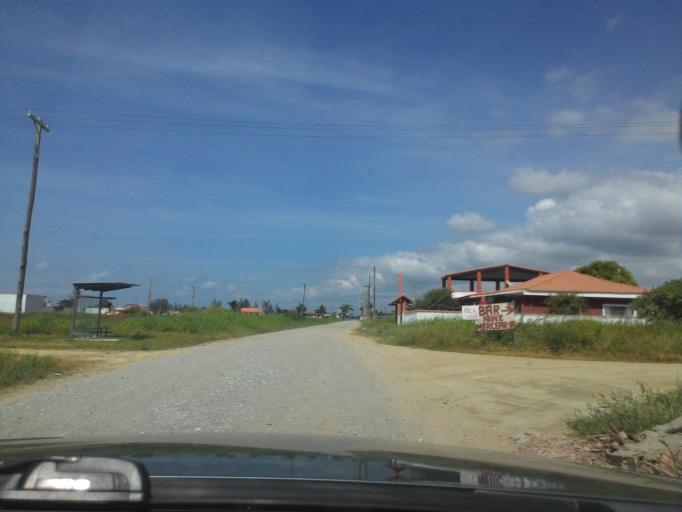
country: BR
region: Sao Paulo
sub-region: Iguape
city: Iguape
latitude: -24.8463
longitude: -47.6931
